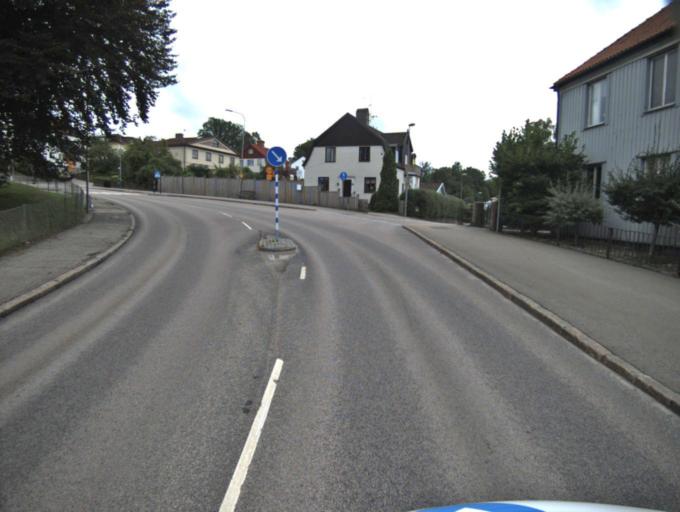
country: SE
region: Vaestra Goetaland
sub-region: Ulricehamns Kommun
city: Ulricehamn
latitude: 57.7880
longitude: 13.4134
